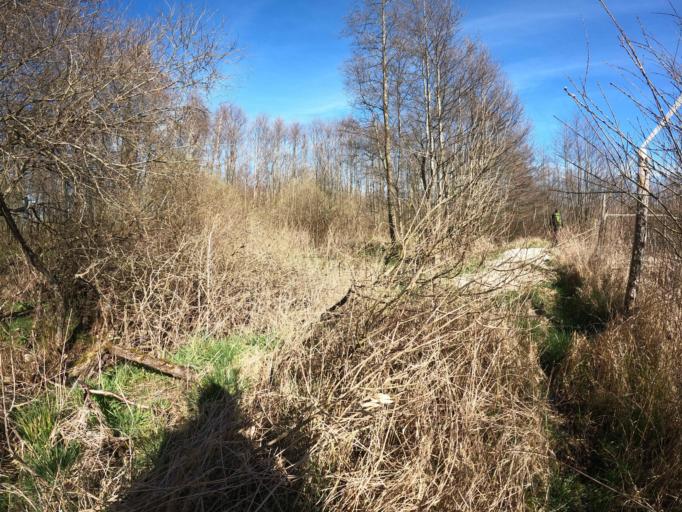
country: PL
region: West Pomeranian Voivodeship
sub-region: Powiat gryficki
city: Brojce
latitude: 53.9259
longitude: 15.2951
